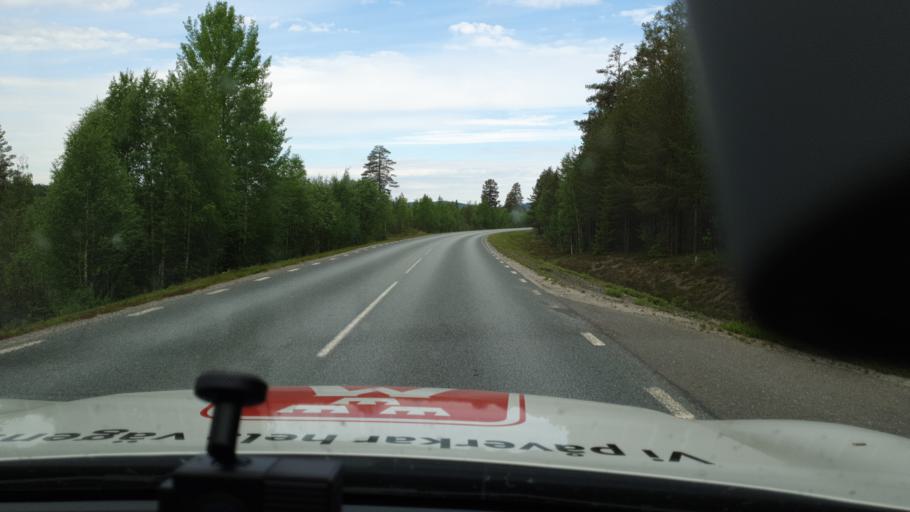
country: SE
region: Vaesterbotten
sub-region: Mala Kommun
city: Mala
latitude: 65.0492
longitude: 18.3991
